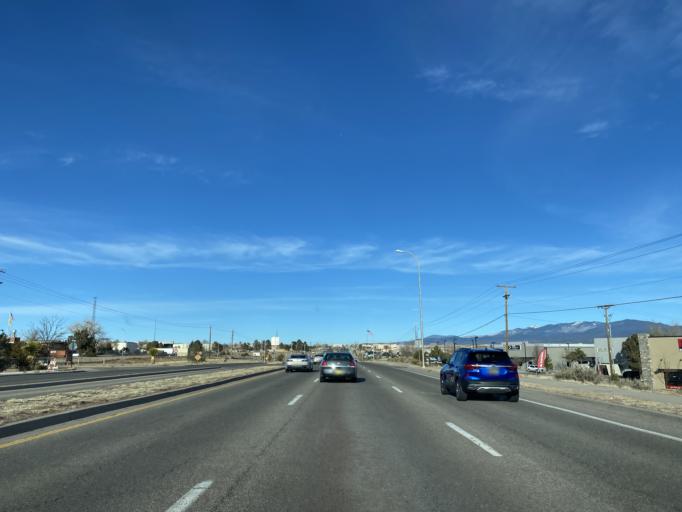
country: US
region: New Mexico
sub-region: Santa Fe County
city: Agua Fria
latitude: 35.6238
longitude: -106.0266
